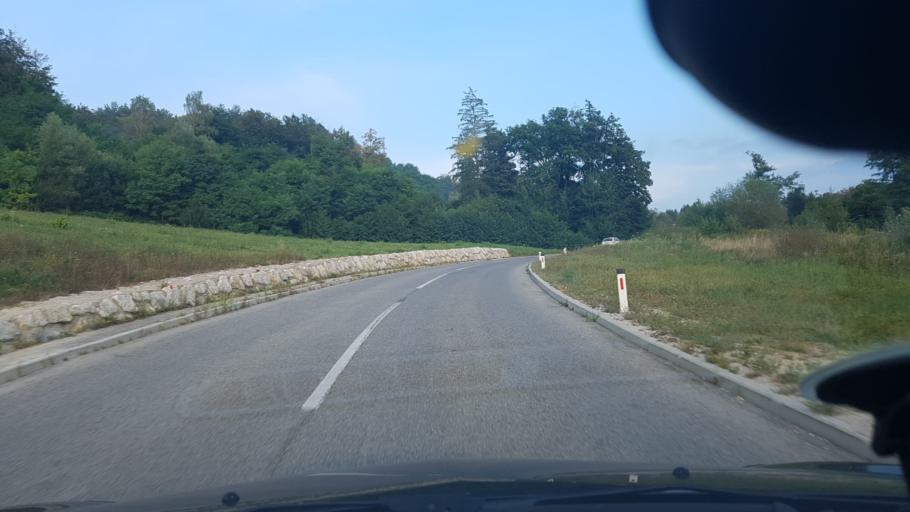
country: SI
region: Kozje
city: Kozje
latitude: 46.0736
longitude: 15.5653
